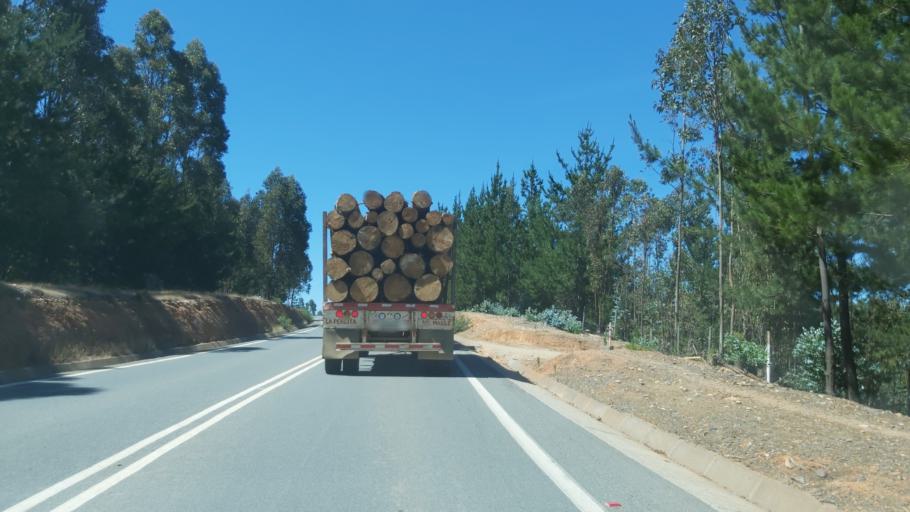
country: CL
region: Maule
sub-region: Provincia de Talca
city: Constitucion
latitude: -34.9319
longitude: -71.9865
